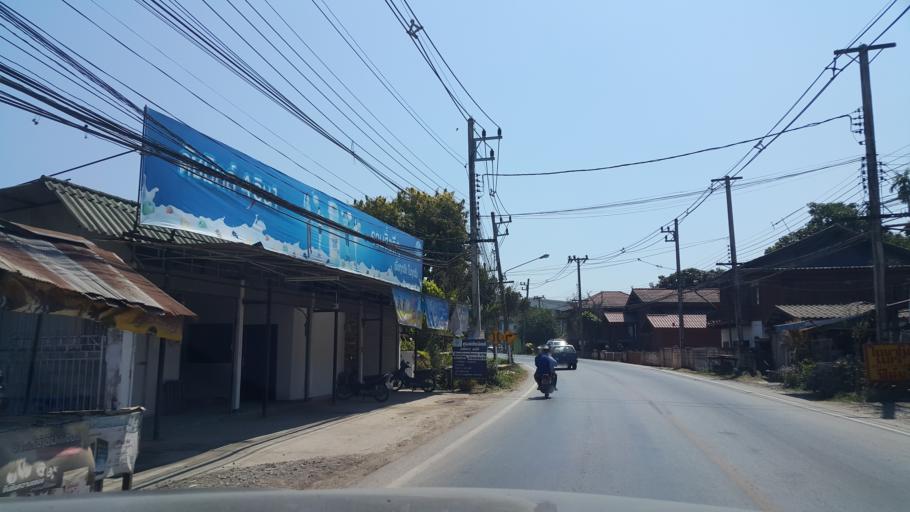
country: TH
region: Chiang Mai
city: San Sai
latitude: 18.8602
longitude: 99.0525
